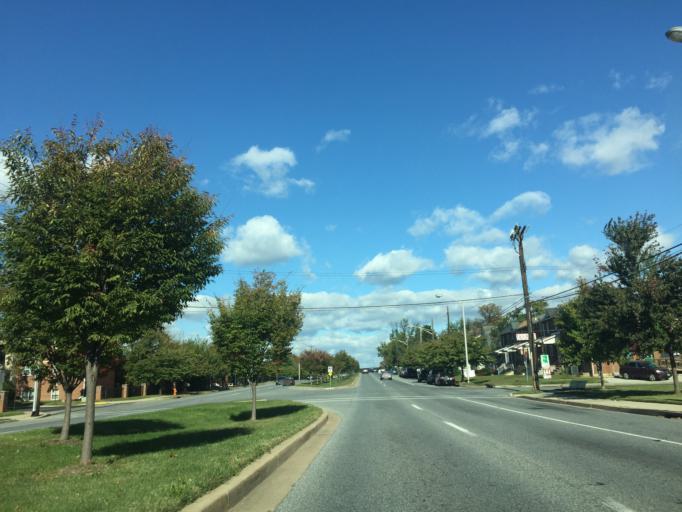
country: US
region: Maryland
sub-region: Baltimore County
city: Dundalk
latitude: 39.2662
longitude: -76.5279
